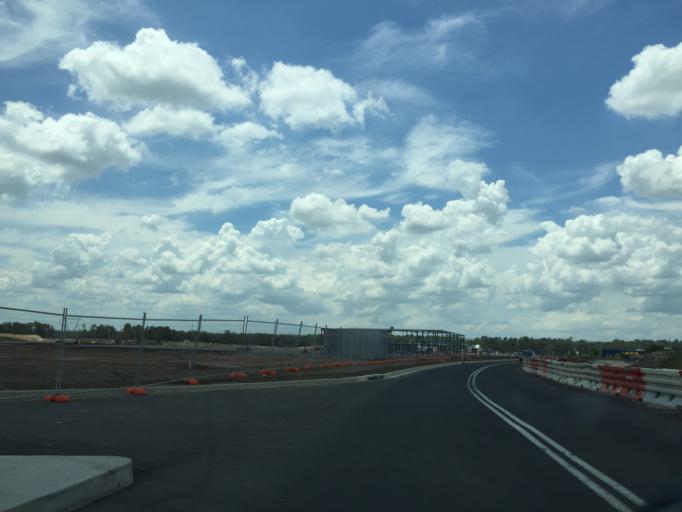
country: AU
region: New South Wales
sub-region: Blacktown
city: Hassall Grove
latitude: -33.7194
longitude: 150.8360
